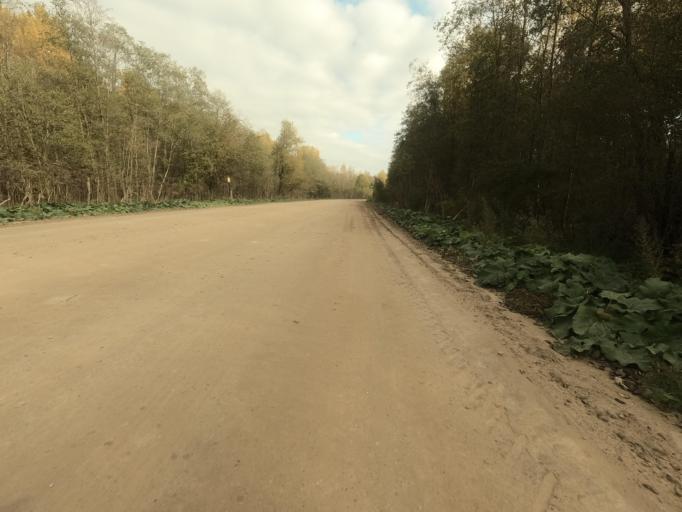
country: RU
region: Novgorod
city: Batetskiy
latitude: 58.8012
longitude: 30.6429
